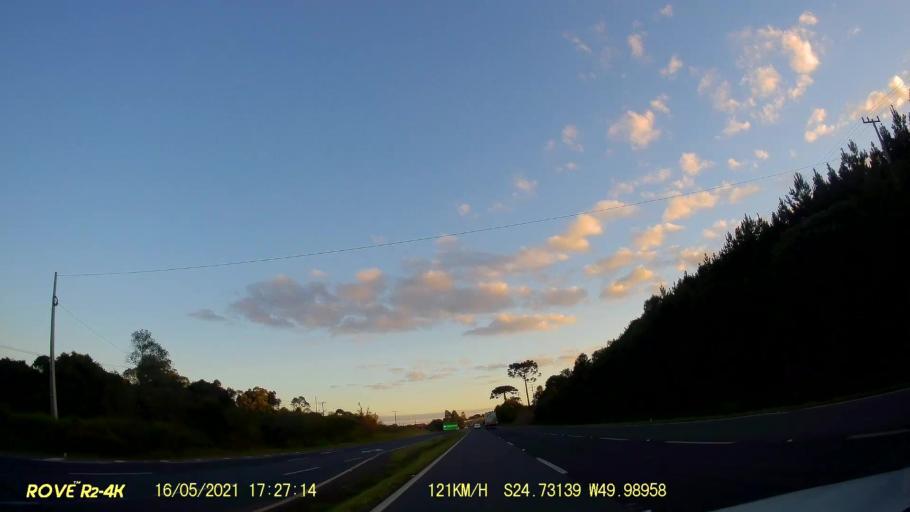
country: BR
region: Parana
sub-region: Castro
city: Castro
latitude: -24.7318
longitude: -49.9898
